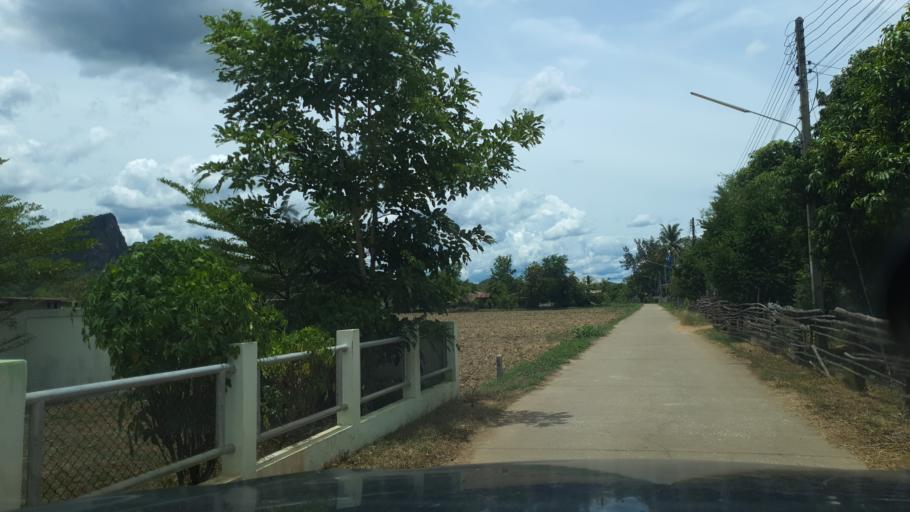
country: TH
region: Sukhothai
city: Thung Saliam
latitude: 17.3270
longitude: 99.5152
